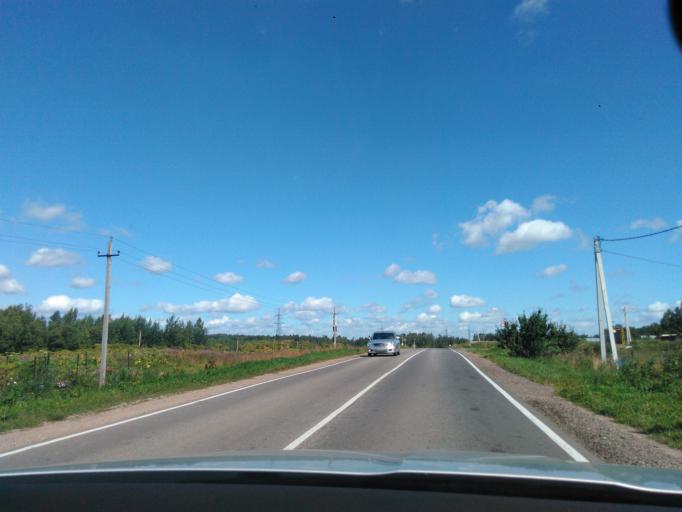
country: RU
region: Moskovskaya
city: Klin
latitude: 56.1977
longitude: 36.8140
